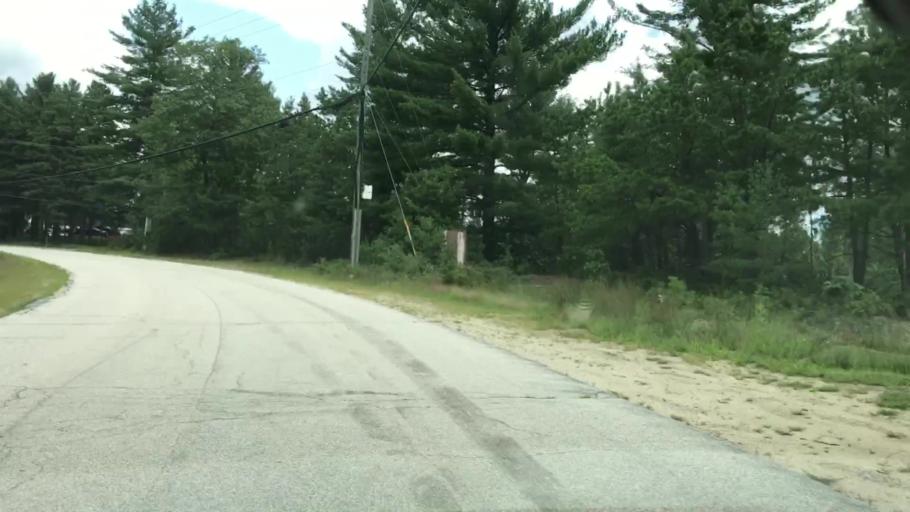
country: US
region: New Hampshire
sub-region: Hillsborough County
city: Hollis
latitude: 42.8067
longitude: -71.5828
